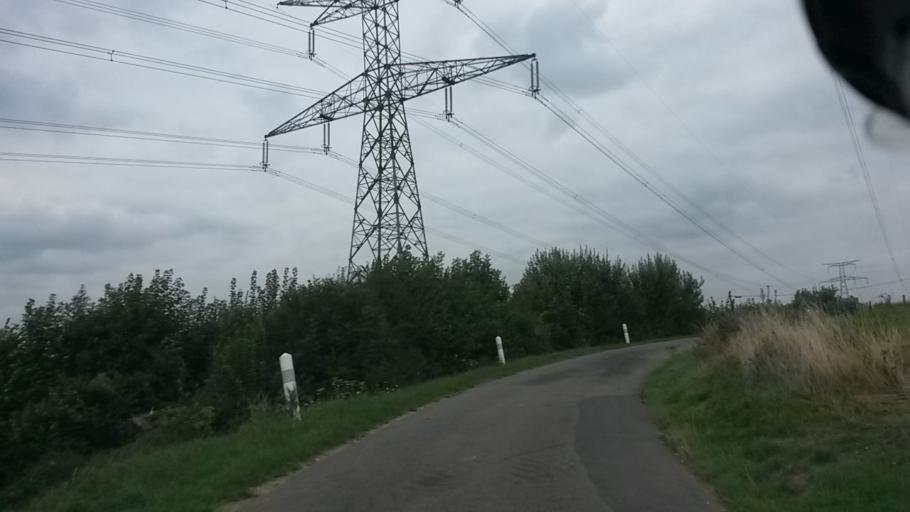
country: FR
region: Haute-Normandie
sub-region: Departement de la Seine-Maritime
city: La Feuillie
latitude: 49.4770
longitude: 1.5284
